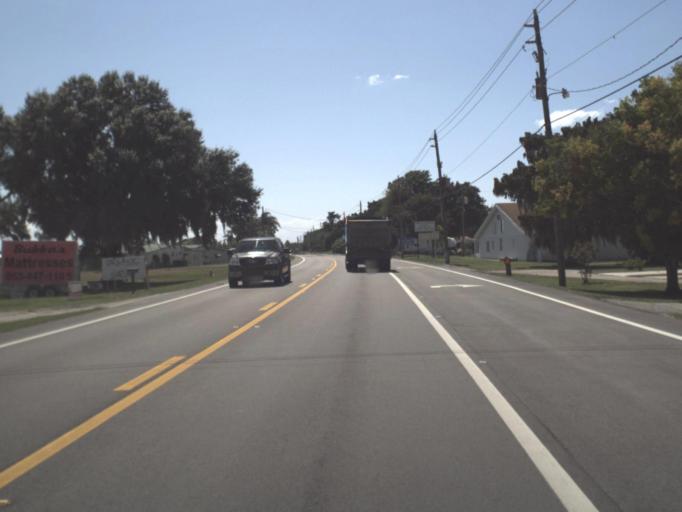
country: US
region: Florida
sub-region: Glades County
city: Buckhead Ridge
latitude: 27.1637
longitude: -80.8621
